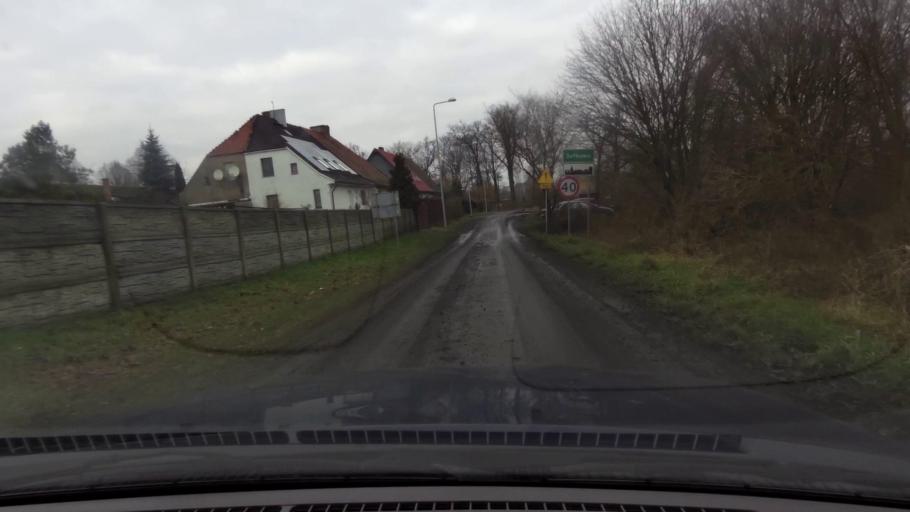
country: PL
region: West Pomeranian Voivodeship
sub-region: Powiat stargardzki
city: Stargard Szczecinski
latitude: 53.3304
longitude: 15.1407
